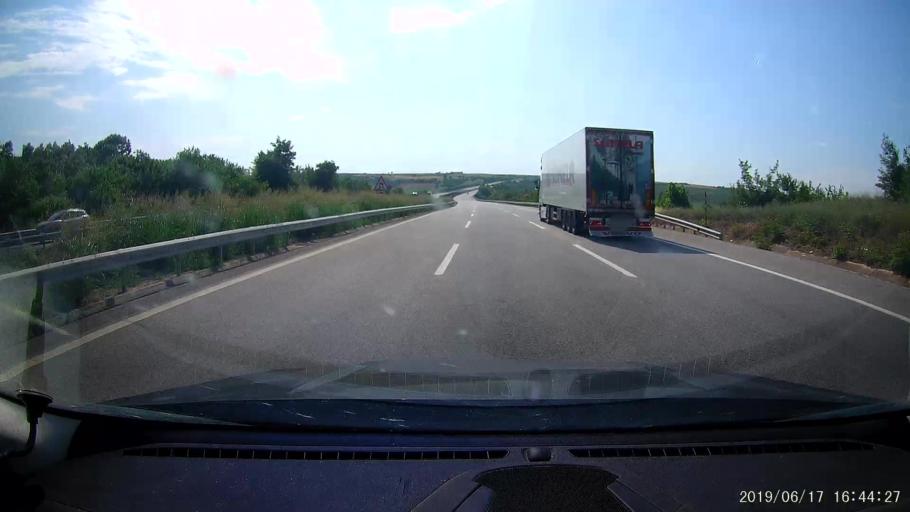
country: TR
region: Kirklareli
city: Luleburgaz
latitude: 41.4815
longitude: 27.2607
